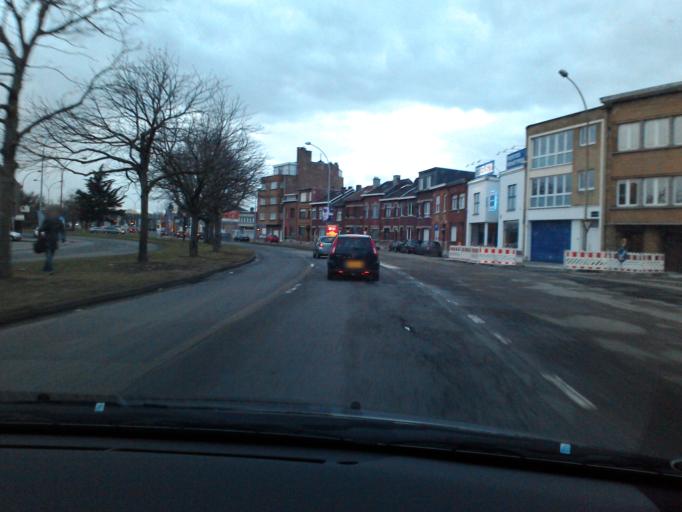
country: BE
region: Wallonia
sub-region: Province de Liege
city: Liege
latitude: 50.6212
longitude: 5.5945
